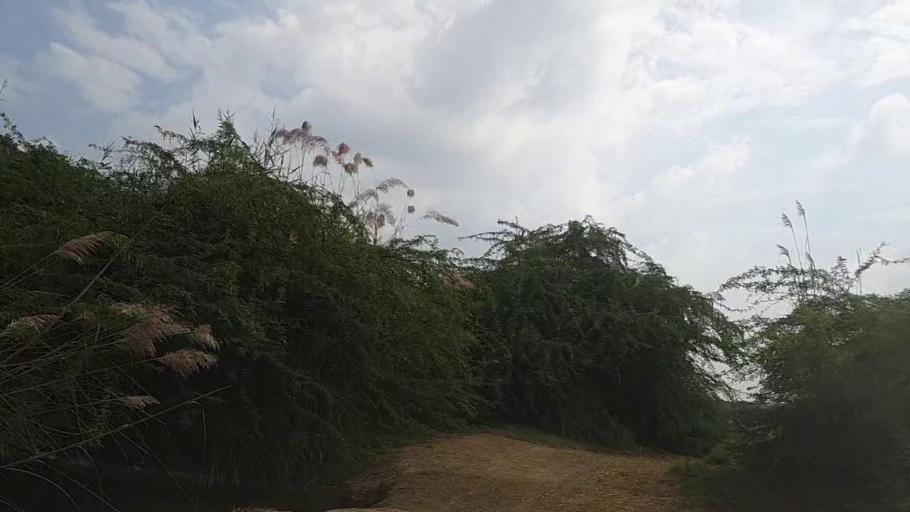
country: PK
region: Sindh
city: Mirpur Batoro
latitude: 24.6099
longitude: 68.1374
